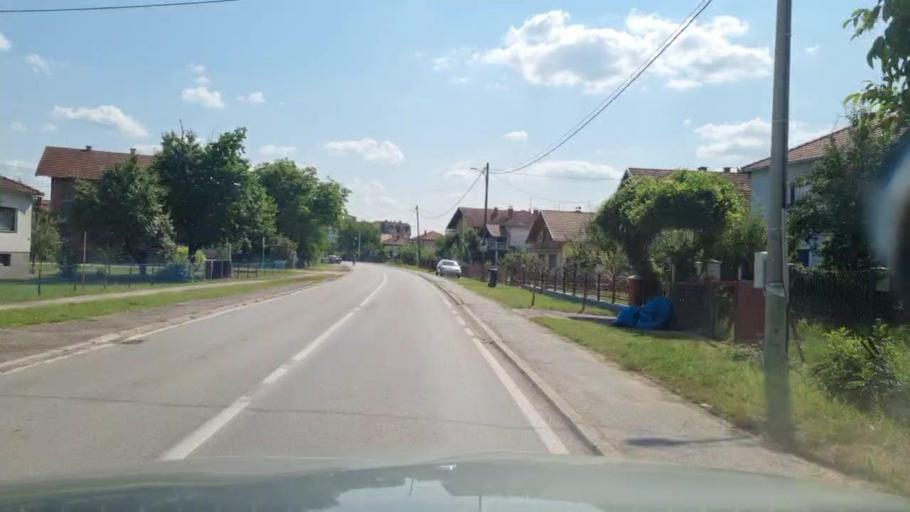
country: BA
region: Federation of Bosnia and Herzegovina
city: Odzak
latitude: 45.0191
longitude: 18.3309
